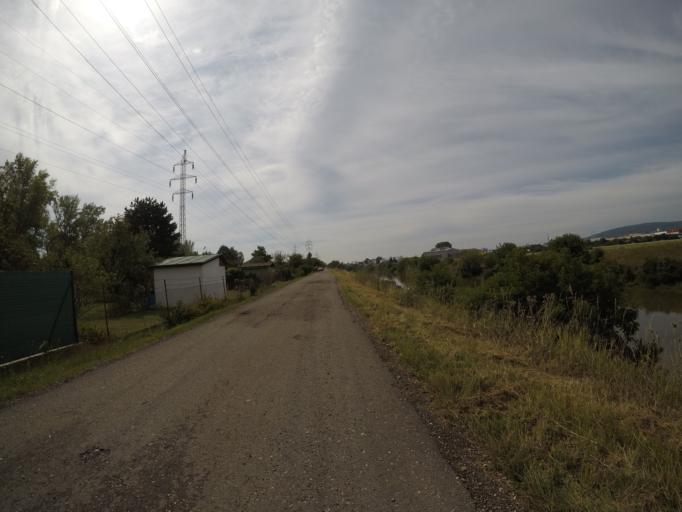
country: SK
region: Trenciansky
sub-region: Okres Nove Mesto nad Vahom
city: Nove Mesto nad Vahom
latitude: 48.7552
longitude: 17.8470
